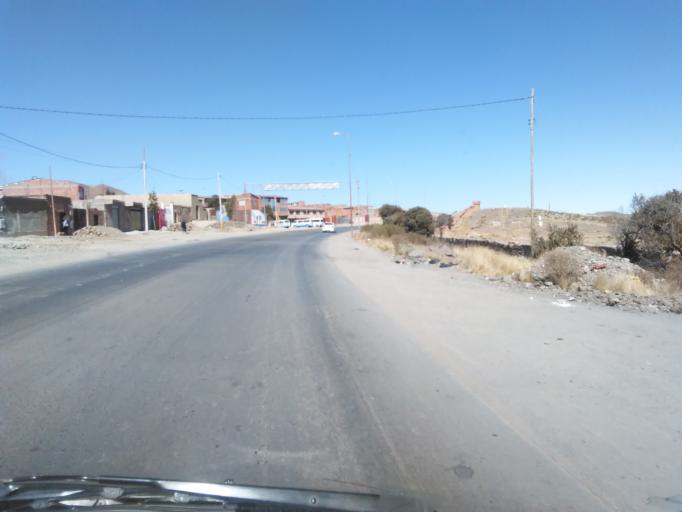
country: BO
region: Oruro
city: Oruro
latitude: -17.9806
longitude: -67.0505
